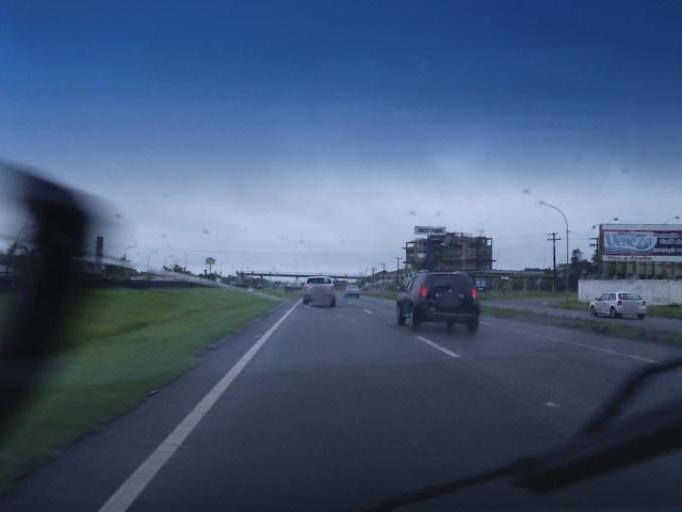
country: BR
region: Sao Paulo
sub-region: Registro
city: Registro
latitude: -24.5328
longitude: -47.8575
